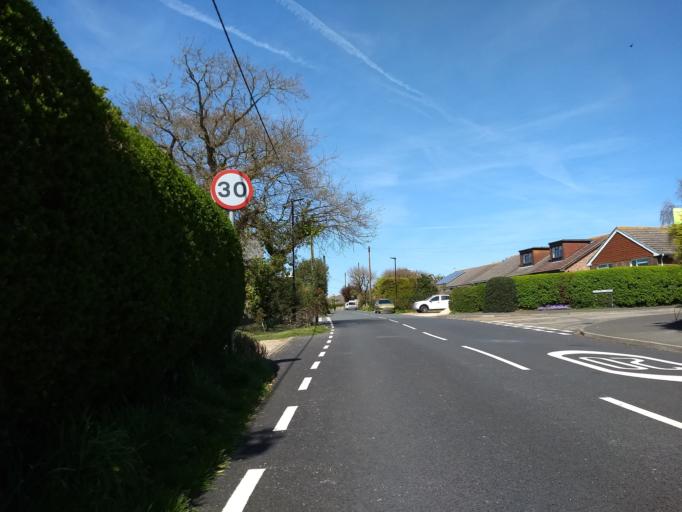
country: GB
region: England
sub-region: Isle of Wight
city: Northwood
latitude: 50.7409
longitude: -1.3137
